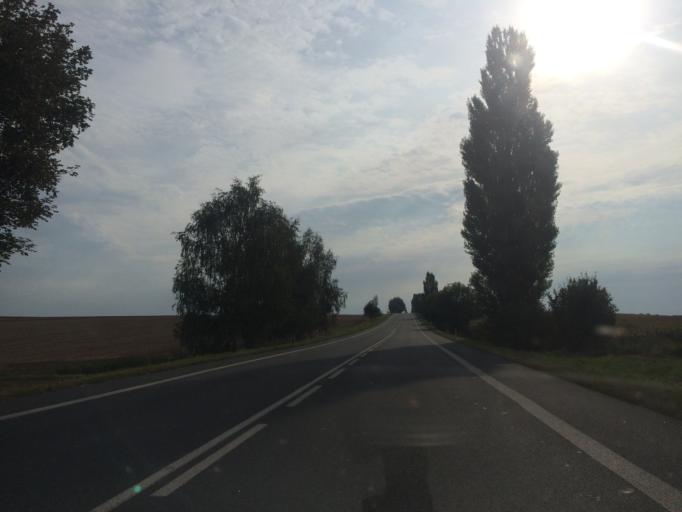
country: CZ
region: Central Bohemia
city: Poricany
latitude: 50.0524
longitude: 14.9160
